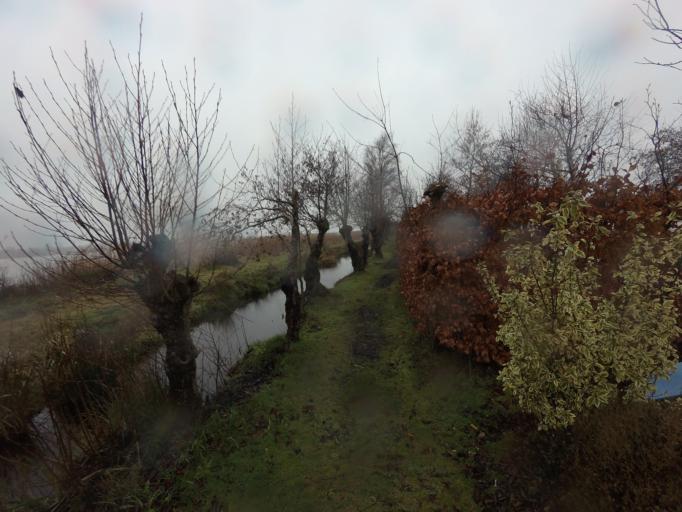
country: NL
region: South Holland
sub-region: Gemeente Vlist
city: Haastrecht
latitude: 52.0218
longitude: 4.7546
